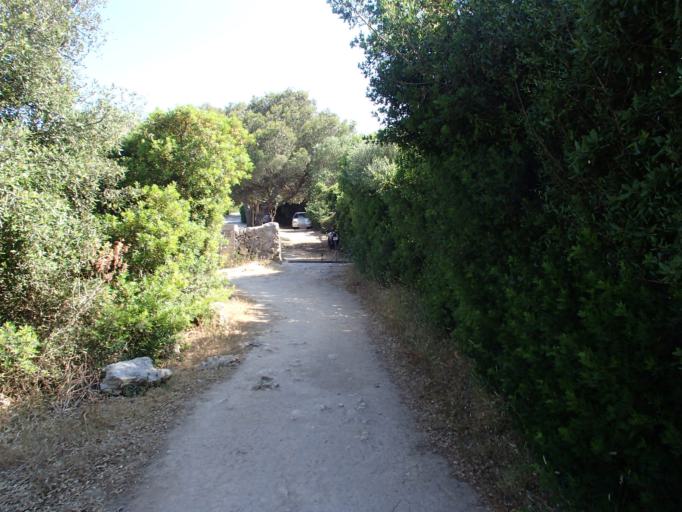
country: ES
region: Balearic Islands
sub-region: Illes Balears
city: Sant Lluis
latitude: 39.8394
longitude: 4.2940
